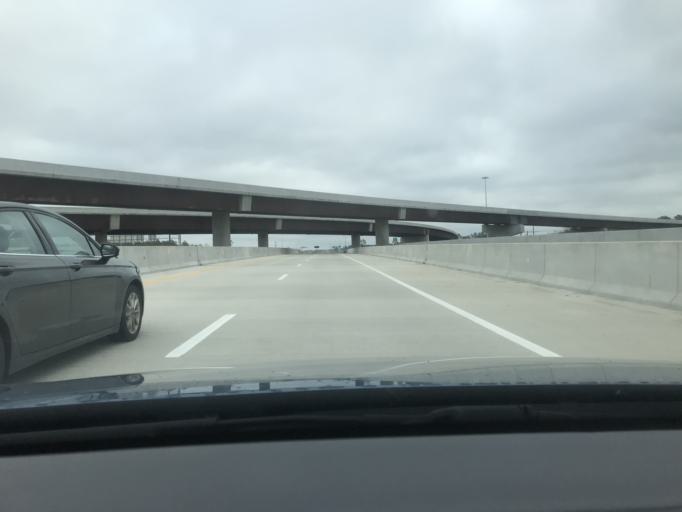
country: US
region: North Carolina
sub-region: Cumberland County
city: Fort Bragg
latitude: 35.1110
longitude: -78.9760
